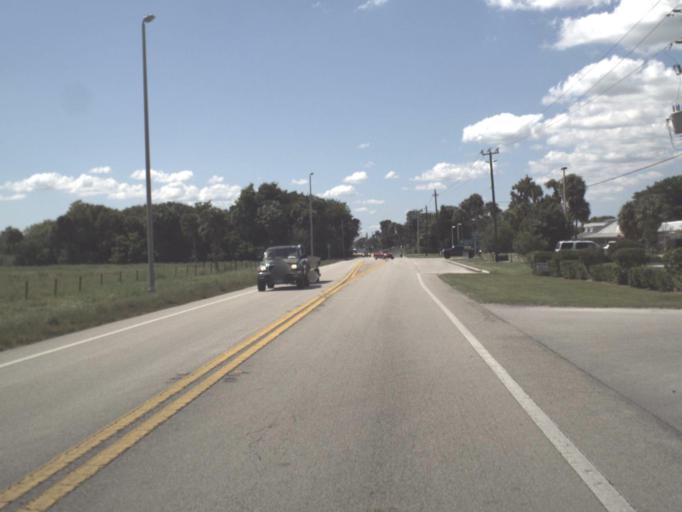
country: US
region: Florida
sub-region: Okeechobee County
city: Taylor Creek
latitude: 27.2076
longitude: -80.8077
